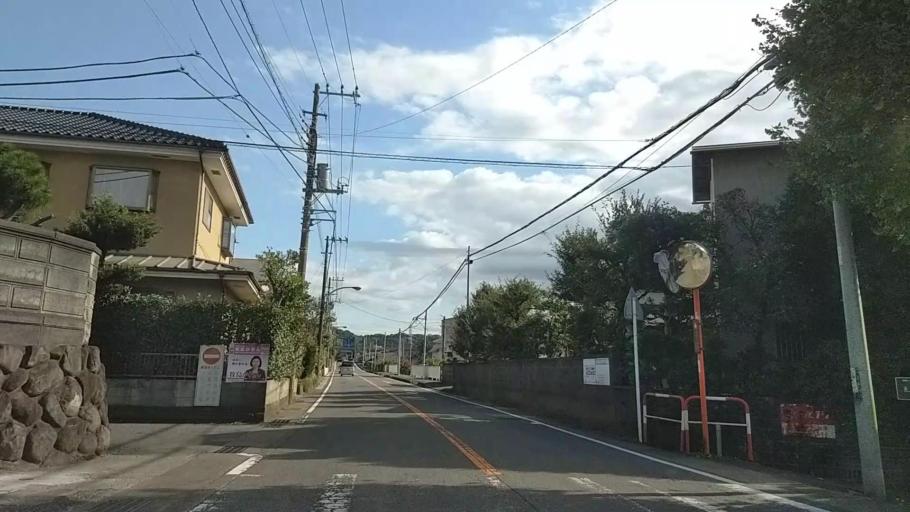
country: JP
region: Kanagawa
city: Odawara
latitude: 35.2937
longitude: 139.1992
